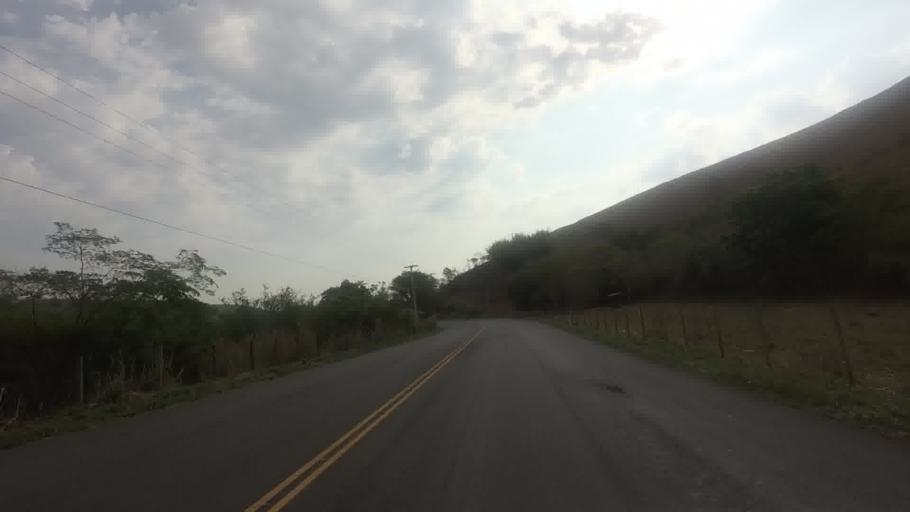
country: BR
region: Rio de Janeiro
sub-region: Itaperuna
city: Itaperuna
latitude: -21.3531
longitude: -41.9152
